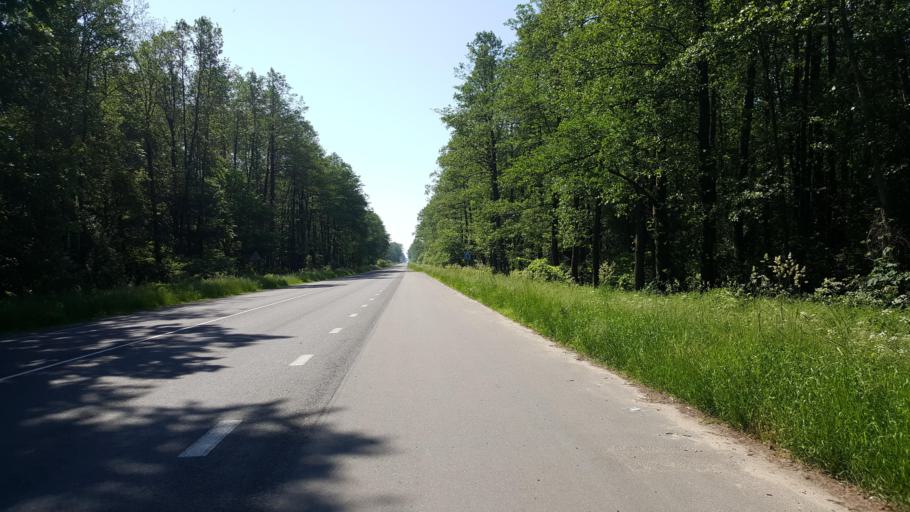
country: BY
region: Brest
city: Zhabinka
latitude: 52.2852
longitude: 23.9450
